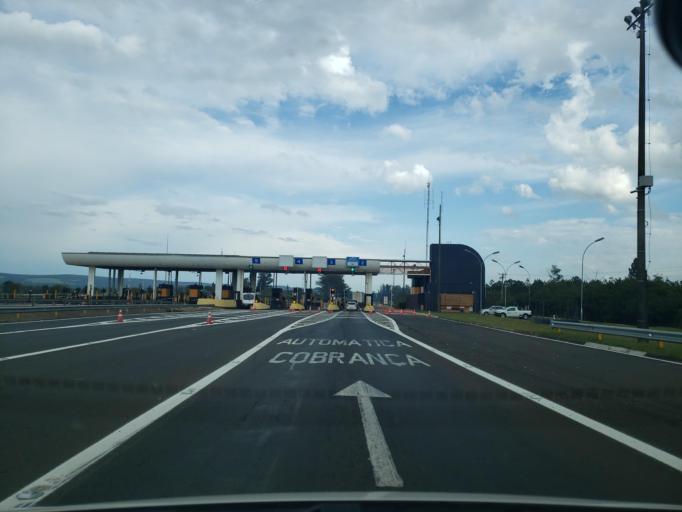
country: BR
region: Sao Paulo
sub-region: Itirapina
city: Itirapina
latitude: -22.2635
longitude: -47.9016
